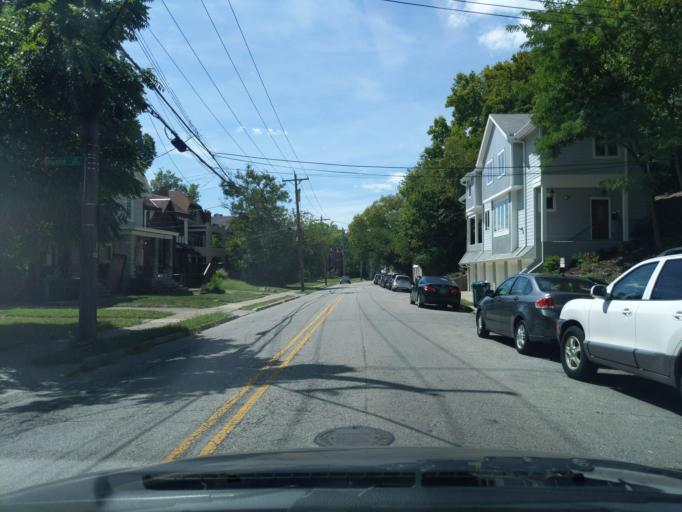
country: US
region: Ohio
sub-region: Hamilton County
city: Saint Bernard
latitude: 39.1345
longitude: -84.5239
